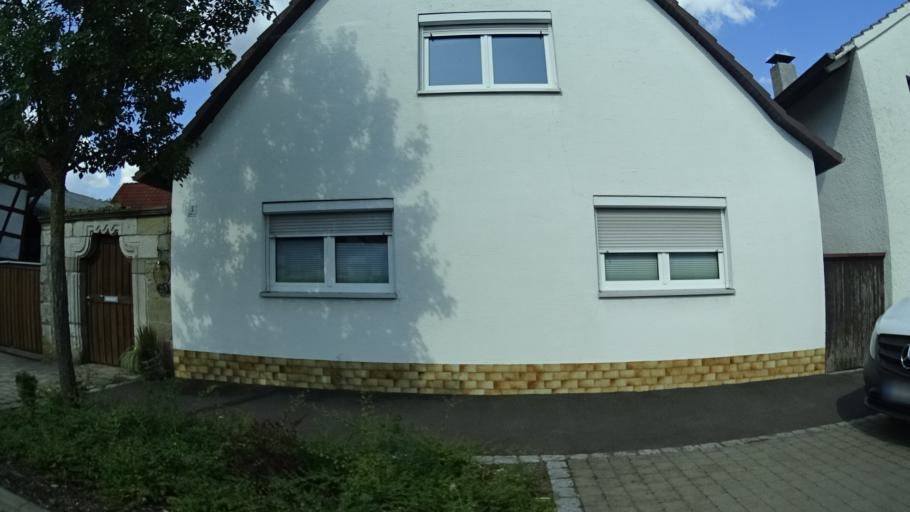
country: DE
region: Bavaria
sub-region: Regierungsbezirk Unterfranken
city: Bundorf
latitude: 50.2740
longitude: 10.5243
